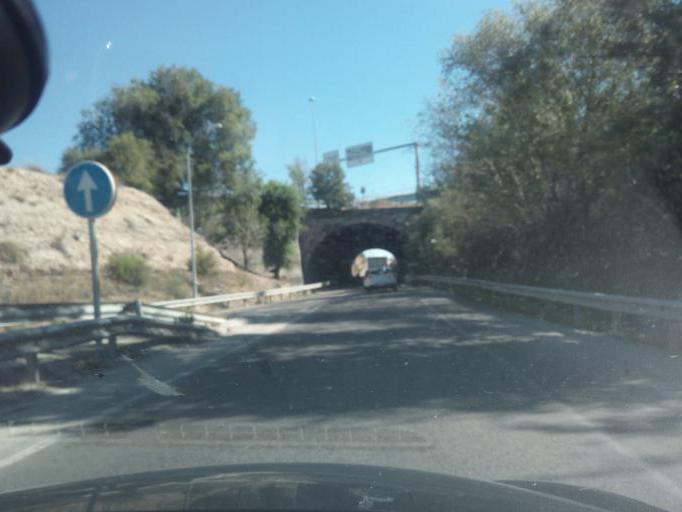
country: ES
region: Madrid
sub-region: Provincia de Madrid
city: San Fernando de Henares
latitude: 40.4516
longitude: -3.5136
